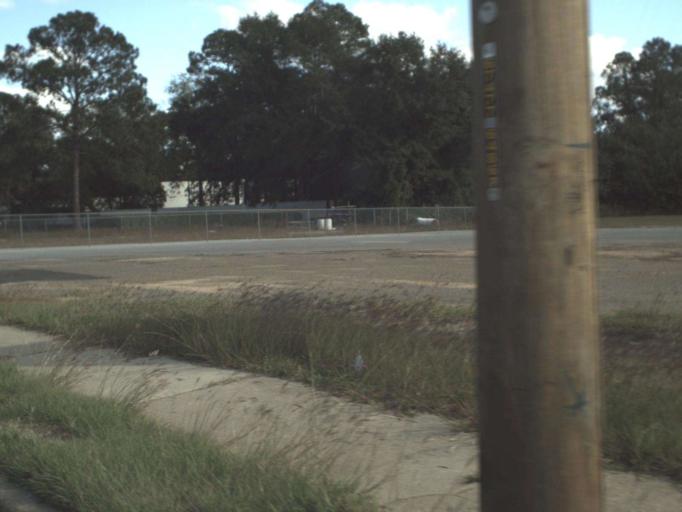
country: US
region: Florida
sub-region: Washington County
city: Chipley
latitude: 30.7797
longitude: -85.5357
